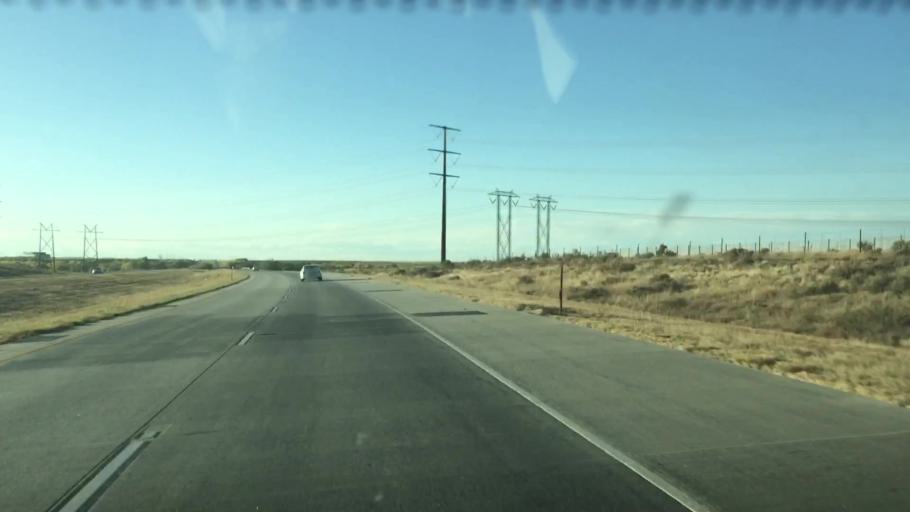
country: US
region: Colorado
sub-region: Arapahoe County
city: Byers
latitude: 39.6648
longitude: -104.0867
